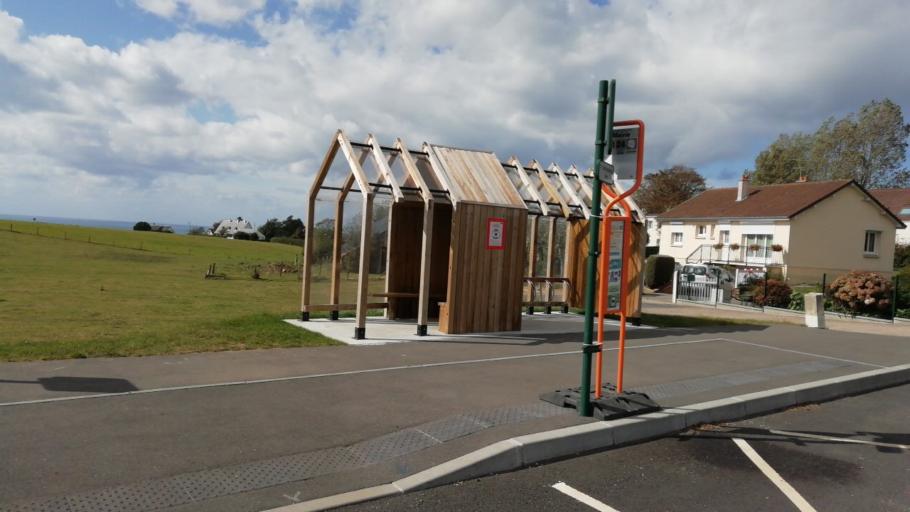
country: FR
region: Haute-Normandie
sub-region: Departement de la Seine-Maritime
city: Saint-Jouin-Bruneval
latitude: 49.6413
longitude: 0.1641
